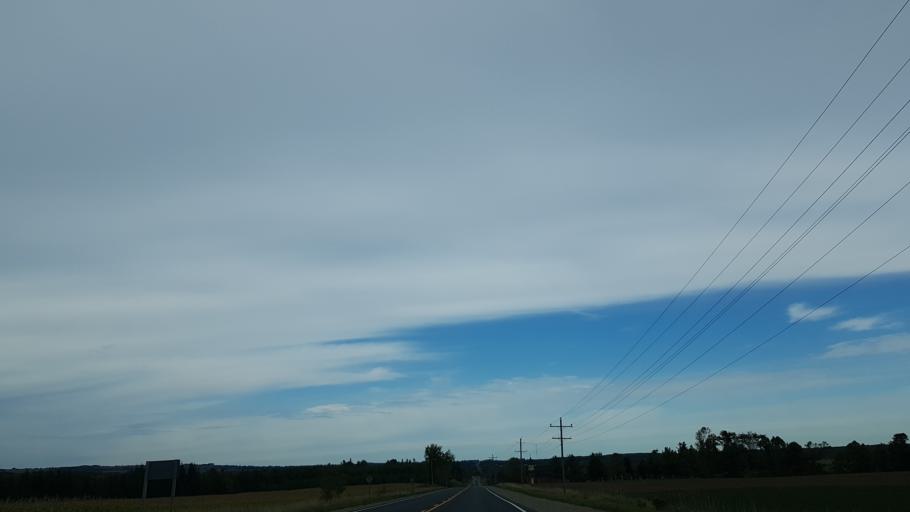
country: CA
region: Ontario
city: Angus
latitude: 44.2903
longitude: -80.0679
